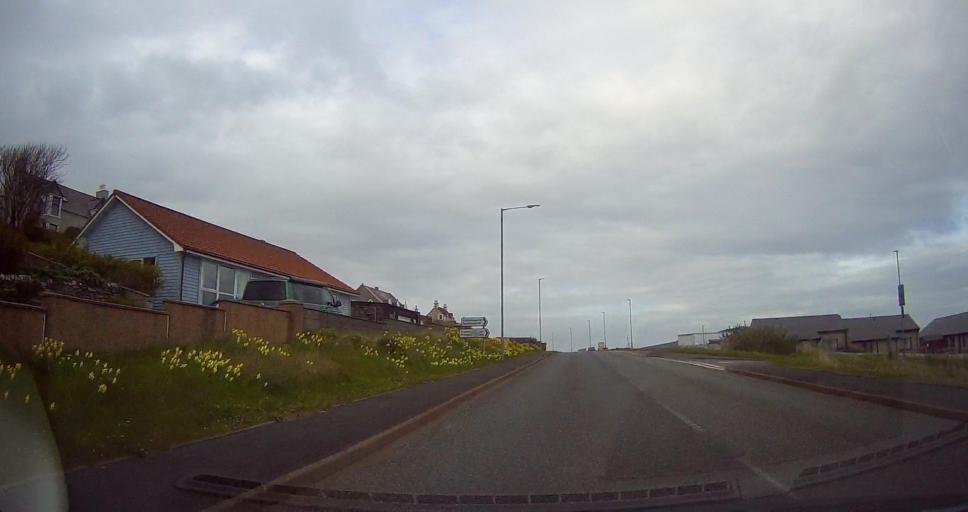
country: GB
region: Scotland
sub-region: Shetland Islands
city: Sandwick
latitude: 60.0440
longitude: -1.2288
